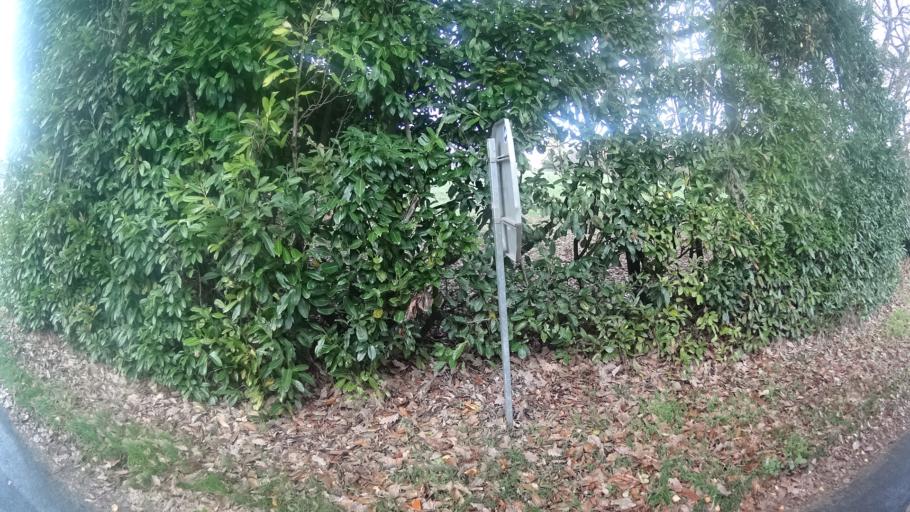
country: FR
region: Pays de la Loire
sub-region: Departement de la Loire-Atlantique
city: Avessac
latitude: 47.6506
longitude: -1.9825
